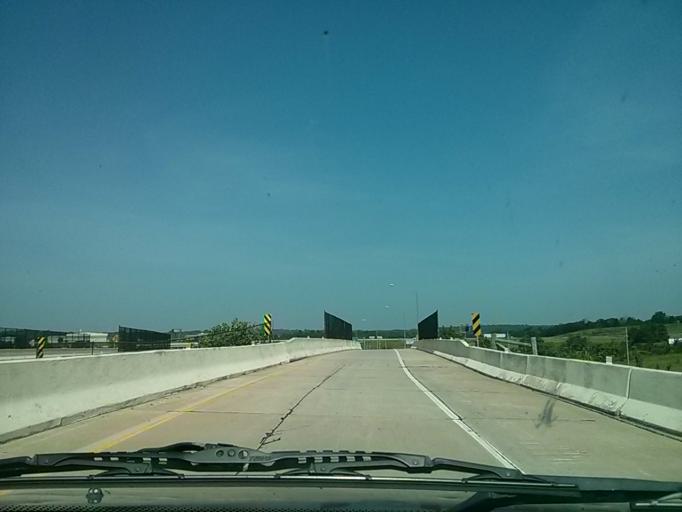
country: US
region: Oklahoma
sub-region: Creek County
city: Sapulpa
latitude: 36.0287
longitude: -96.0840
